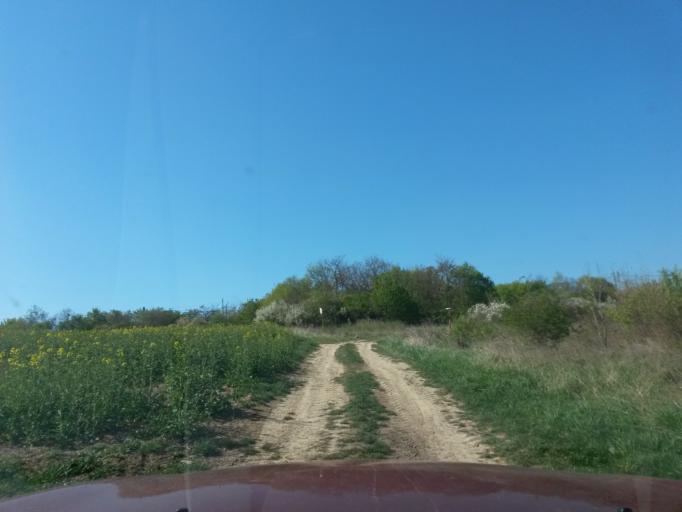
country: SK
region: Kosicky
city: Secovce
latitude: 48.6150
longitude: 21.5417
